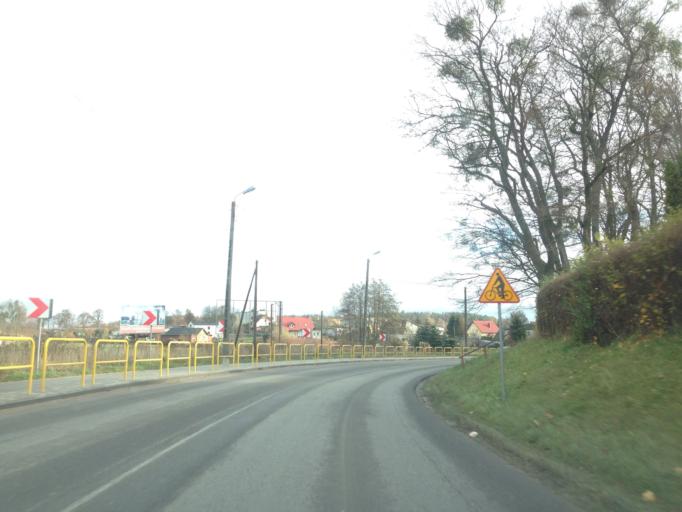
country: PL
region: Pomeranian Voivodeship
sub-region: Powiat gdanski
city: Lublewo Gdanskie
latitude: 54.2931
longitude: 18.5272
